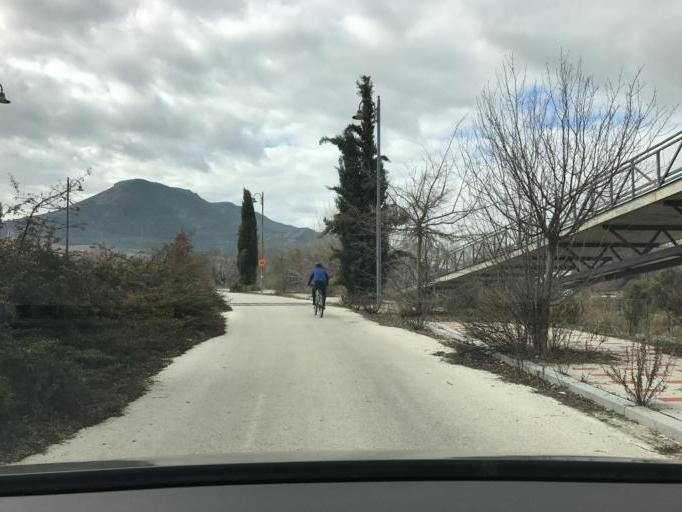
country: ES
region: Andalusia
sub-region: Provincia de Granada
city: Atarfe
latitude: 37.2683
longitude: -3.6888
